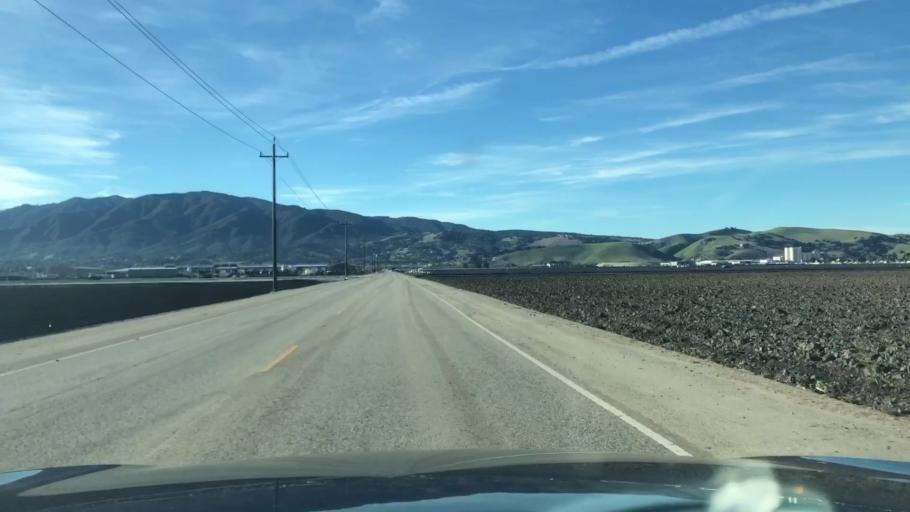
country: US
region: California
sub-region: Monterey County
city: Salinas
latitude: 36.6308
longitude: -121.6251
